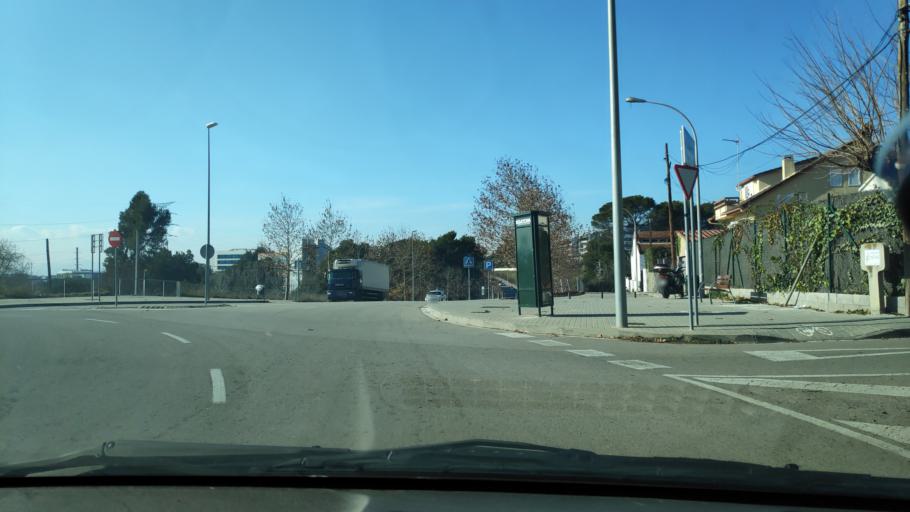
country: ES
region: Catalonia
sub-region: Provincia de Barcelona
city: Sant Cugat del Valles
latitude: 41.4928
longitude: 2.0814
